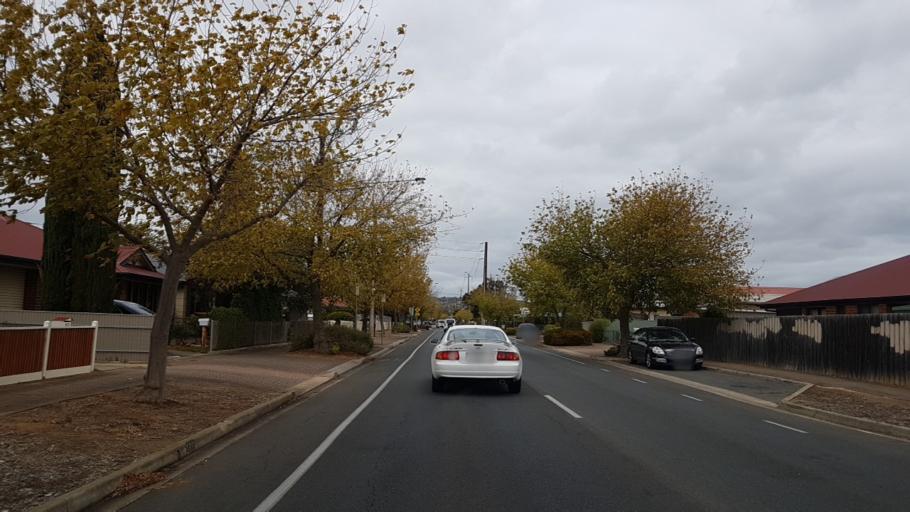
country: AU
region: South Australia
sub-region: Marion
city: Clovelly Park
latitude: -35.0065
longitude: 138.5658
